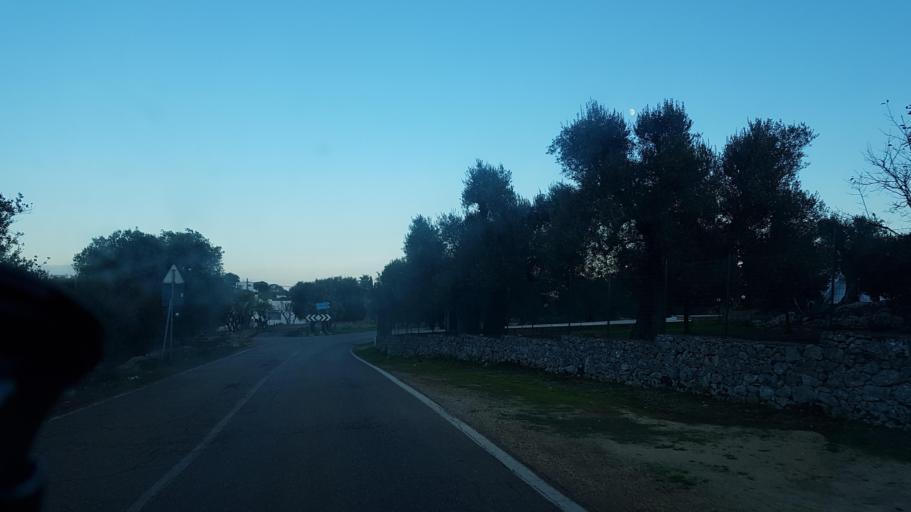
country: IT
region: Apulia
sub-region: Provincia di Brindisi
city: Ostuni
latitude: 40.6957
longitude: 17.5941
